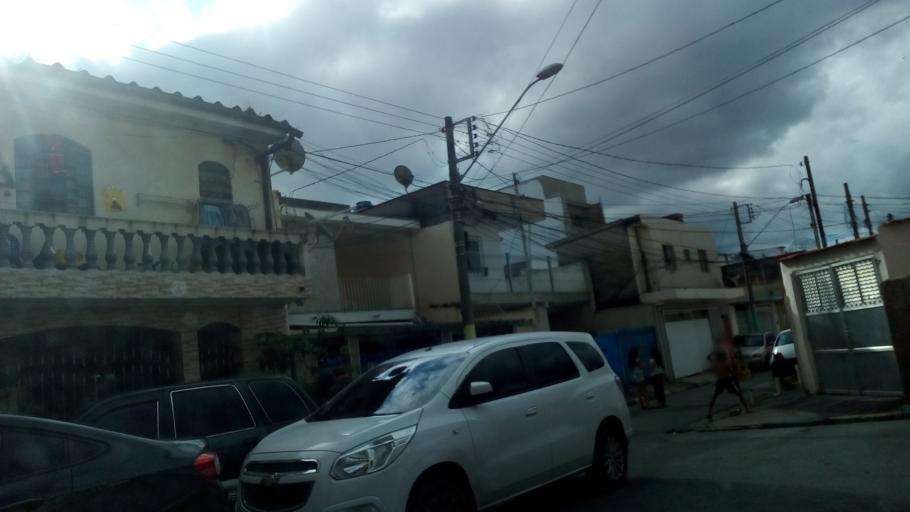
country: BR
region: Sao Paulo
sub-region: Guarulhos
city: Guarulhos
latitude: -23.4619
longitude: -46.5181
